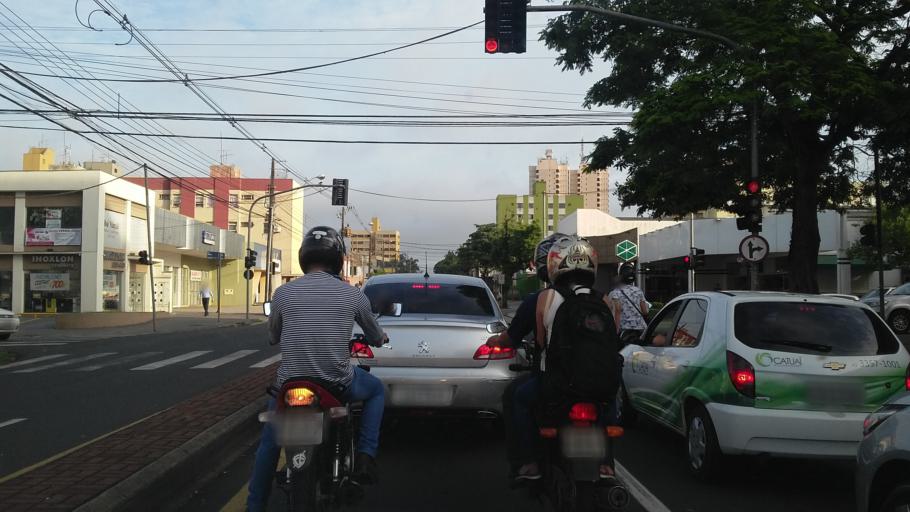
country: BR
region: Parana
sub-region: Londrina
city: Londrina
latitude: -23.3066
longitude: -51.1784
